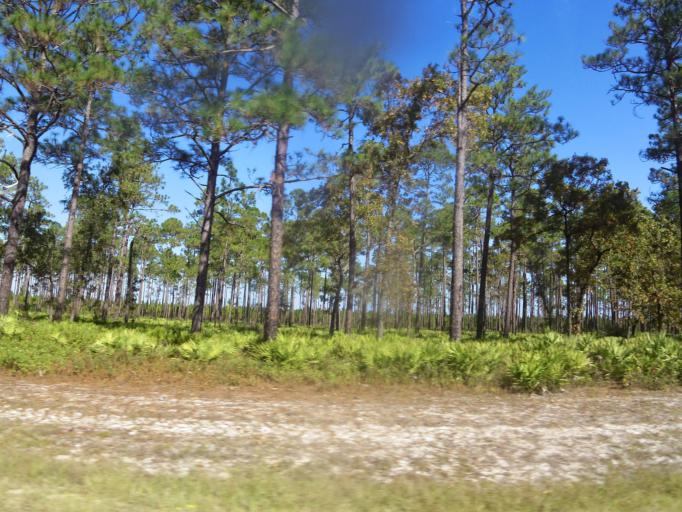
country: US
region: Georgia
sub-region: Charlton County
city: Folkston
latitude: 30.7408
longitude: -82.1236
